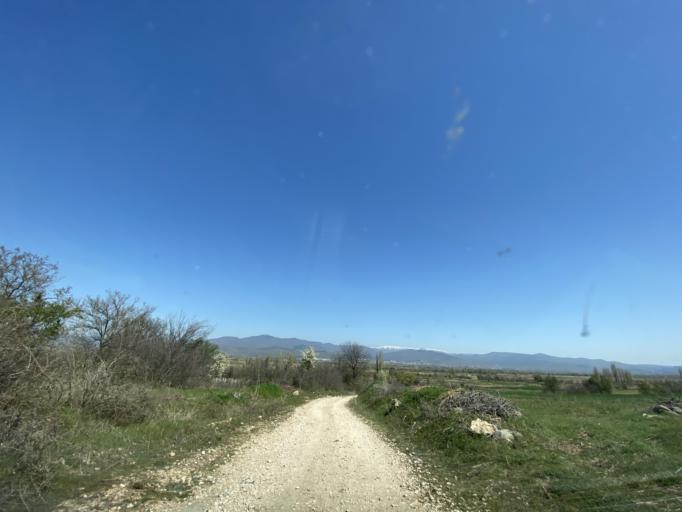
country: MK
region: Zrnovci
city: Zrnovci
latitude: 41.8530
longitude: 22.3896
